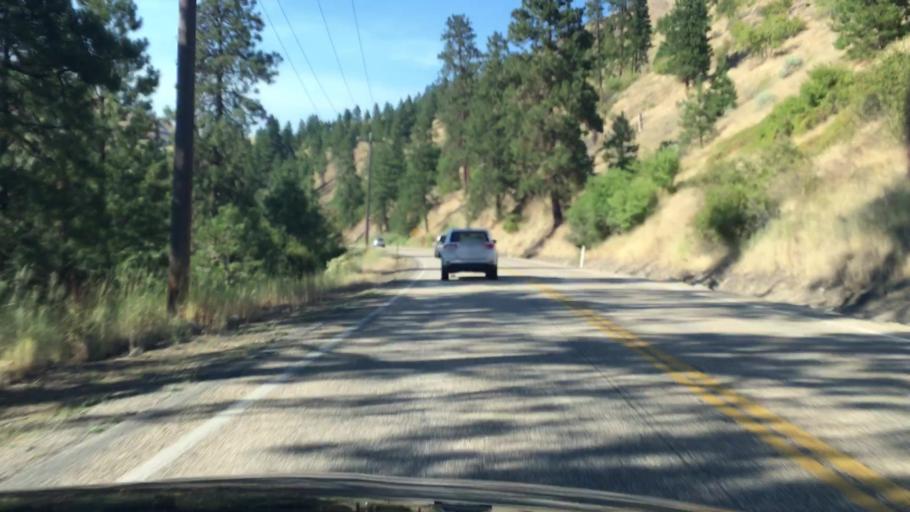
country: US
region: Idaho
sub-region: Boise County
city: Idaho City
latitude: 44.0428
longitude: -116.1310
